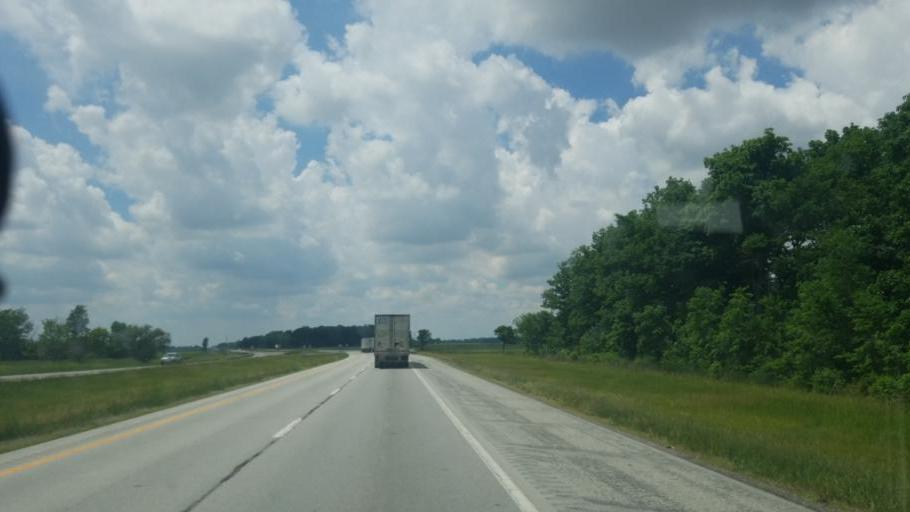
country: US
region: Ohio
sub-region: Allen County
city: Elida
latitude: 40.8376
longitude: -84.2272
